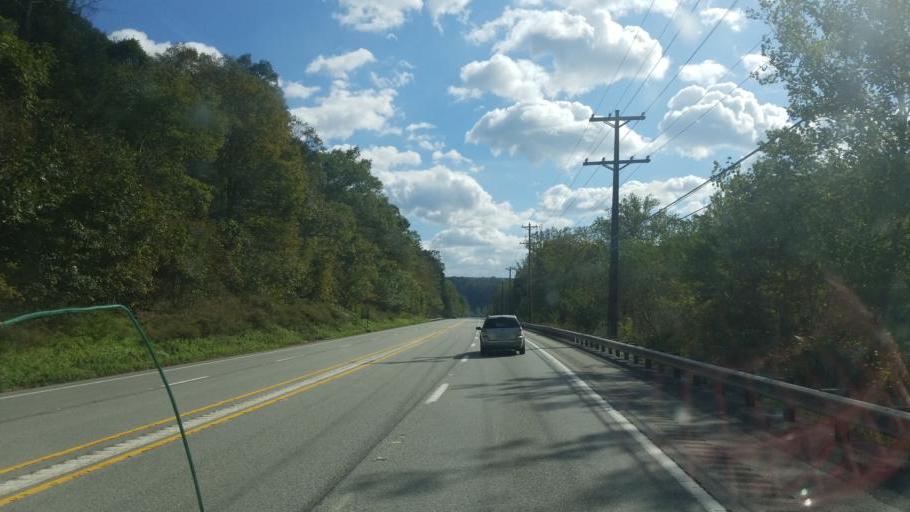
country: US
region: Pennsylvania
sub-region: Bedford County
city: Earlston
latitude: 39.9973
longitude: -78.2892
